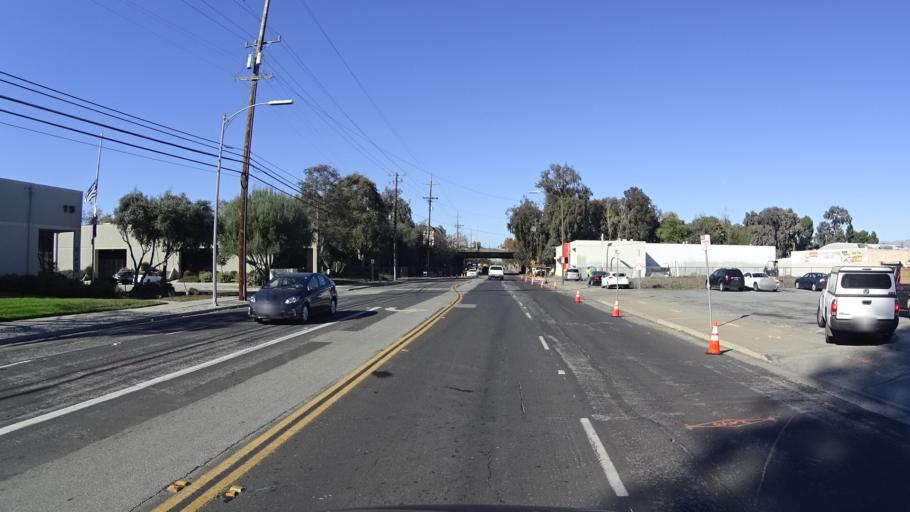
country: US
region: California
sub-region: Santa Clara County
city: San Jose
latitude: 37.3596
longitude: -121.9037
